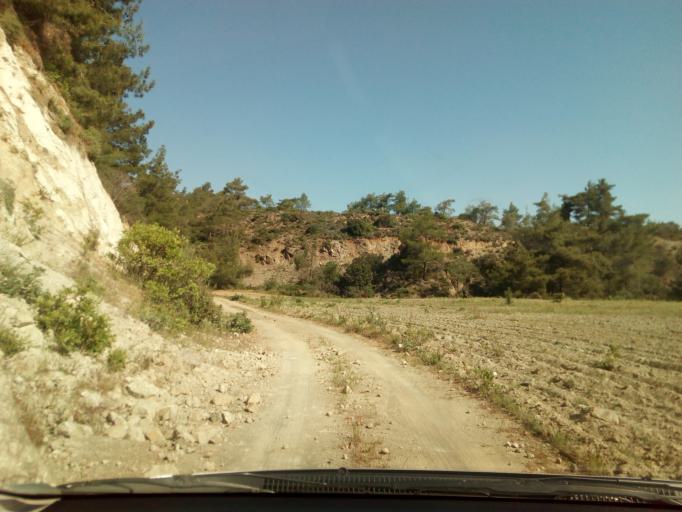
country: CY
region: Limassol
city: Pelendri
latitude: 34.8274
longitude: 33.0508
